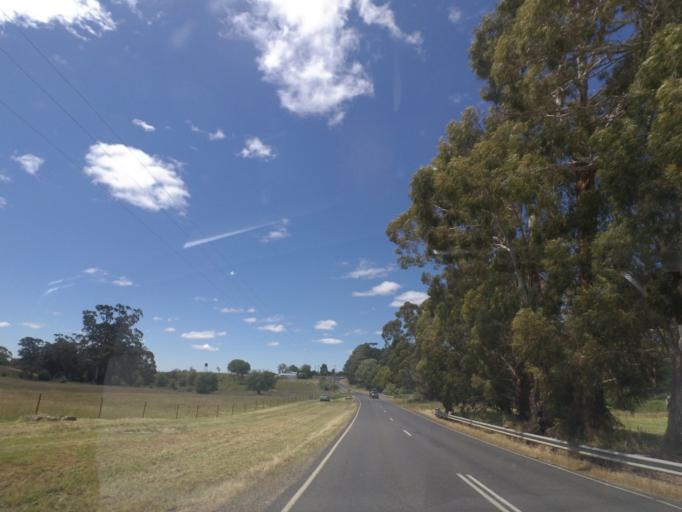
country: AU
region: Victoria
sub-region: Mount Alexander
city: Castlemaine
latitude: -37.3258
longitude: 144.1926
